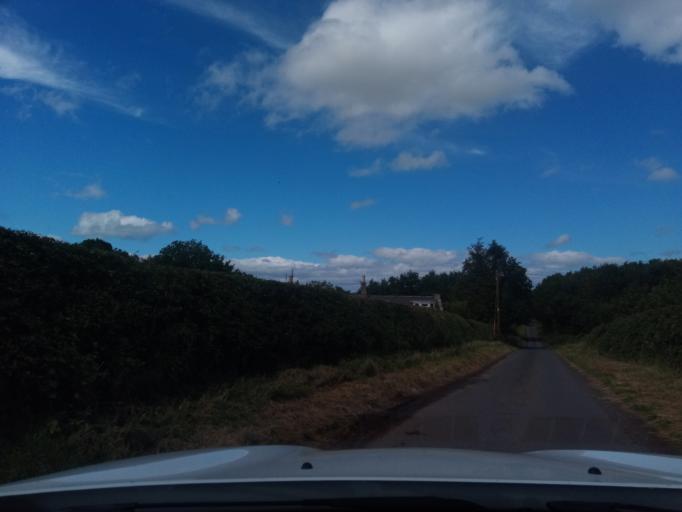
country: GB
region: Scotland
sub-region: The Scottish Borders
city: Saint Boswells
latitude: 55.5648
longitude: -2.5670
